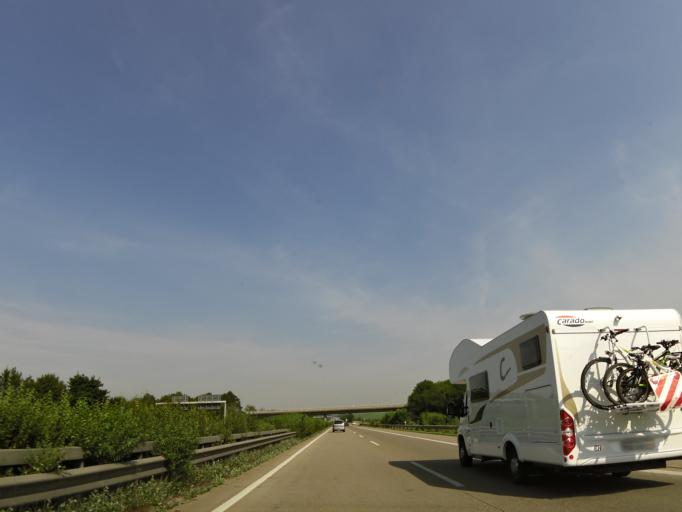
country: DE
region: Rheinland-Pfalz
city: Morstadt
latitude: 49.6666
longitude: 8.2718
